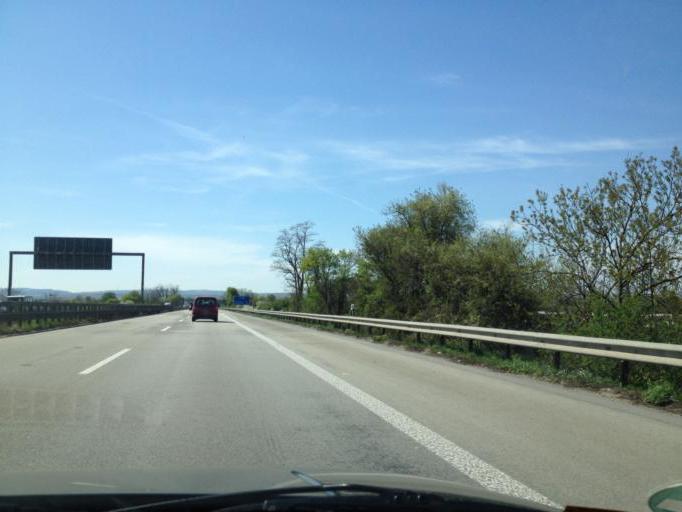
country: DE
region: Rheinland-Pfalz
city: Heuchelheim bei Frankenthal
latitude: 49.5541
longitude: 8.2983
